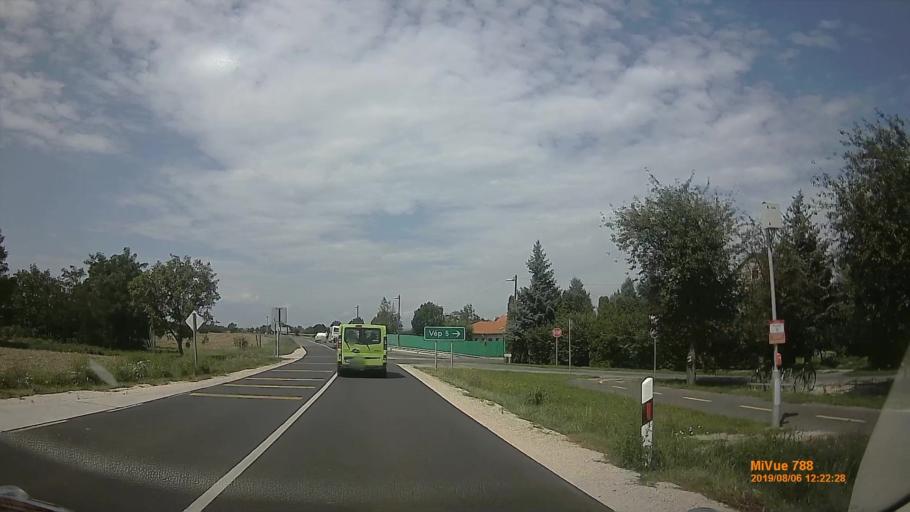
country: HU
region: Vas
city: Taplanszentkereszt
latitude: 47.1882
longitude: 16.7309
